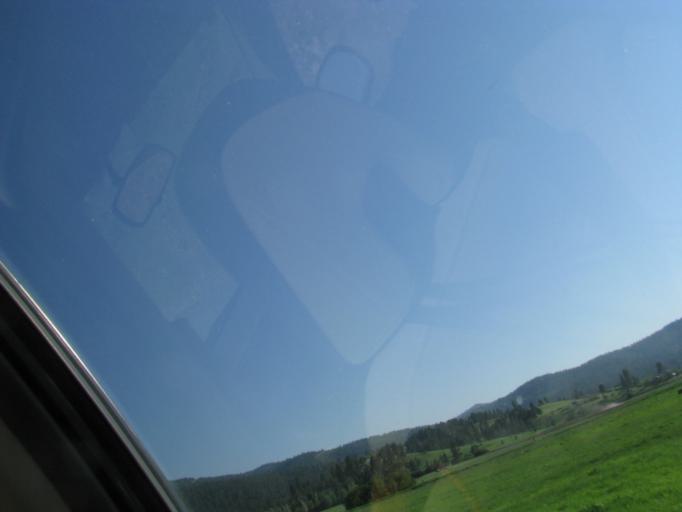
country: US
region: Washington
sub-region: Spokane County
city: Liberty Lake
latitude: 47.6225
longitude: -117.1144
